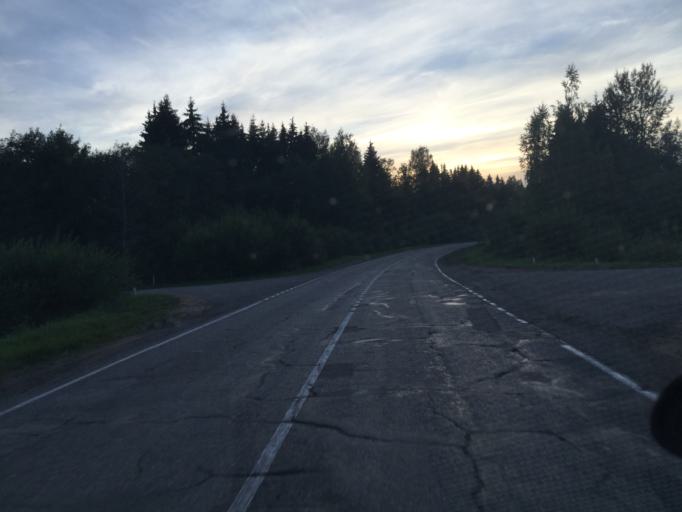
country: RU
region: Pskov
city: Nevel'
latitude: 55.9830
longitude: 30.0067
